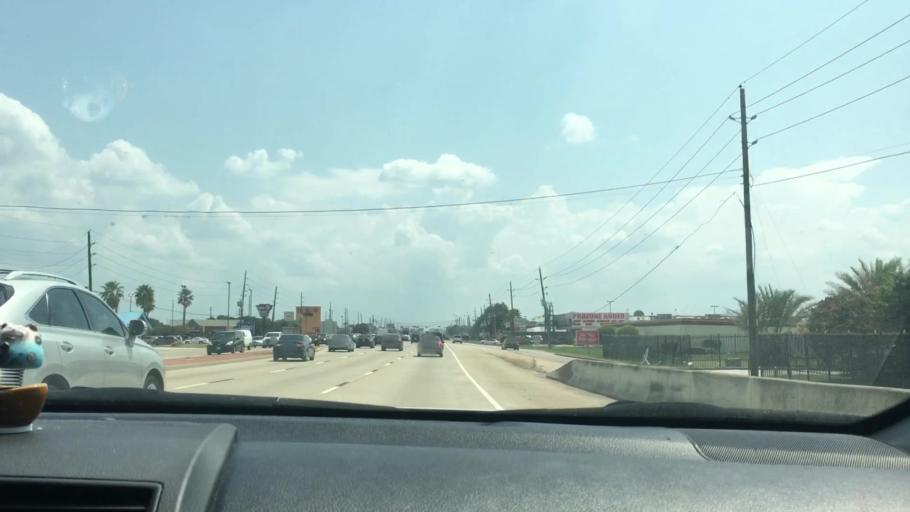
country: US
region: Texas
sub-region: Fort Bend County
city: Mission Bend
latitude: 29.7082
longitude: -95.6442
